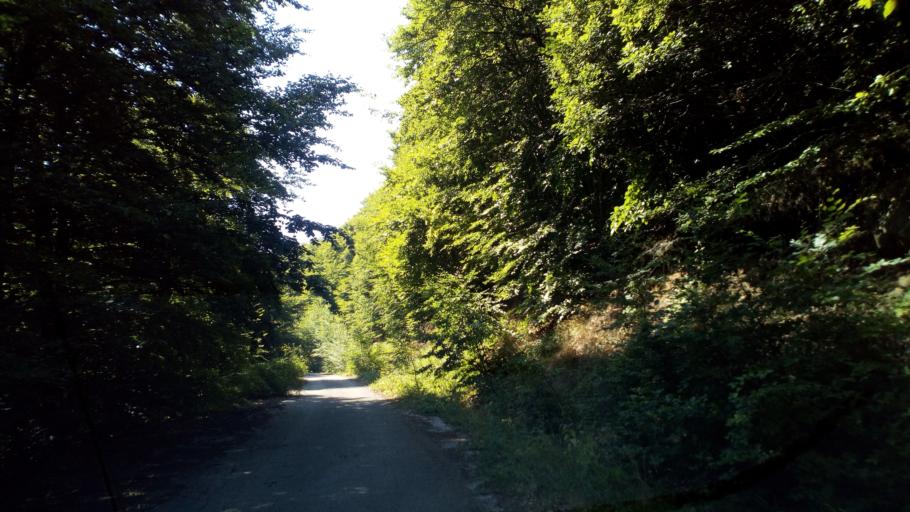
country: GR
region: Central Macedonia
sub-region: Nomos Thessalonikis
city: Sochos
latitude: 40.8279
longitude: 23.3562
